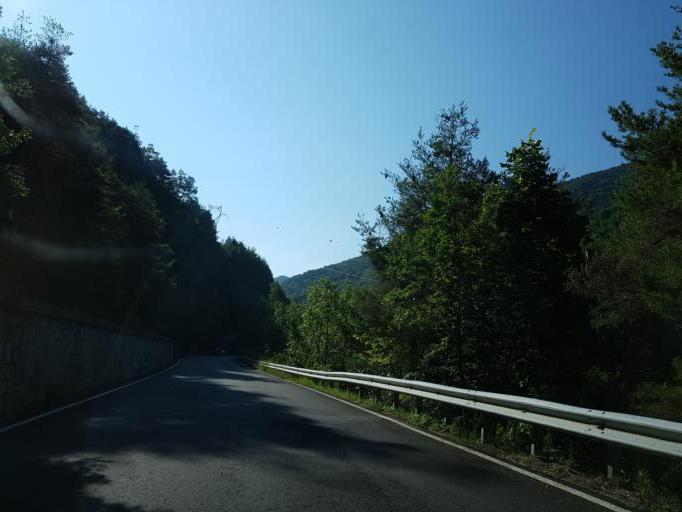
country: IT
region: Piedmont
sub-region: Provincia di Cuneo
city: Macra
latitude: 44.4978
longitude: 7.1957
